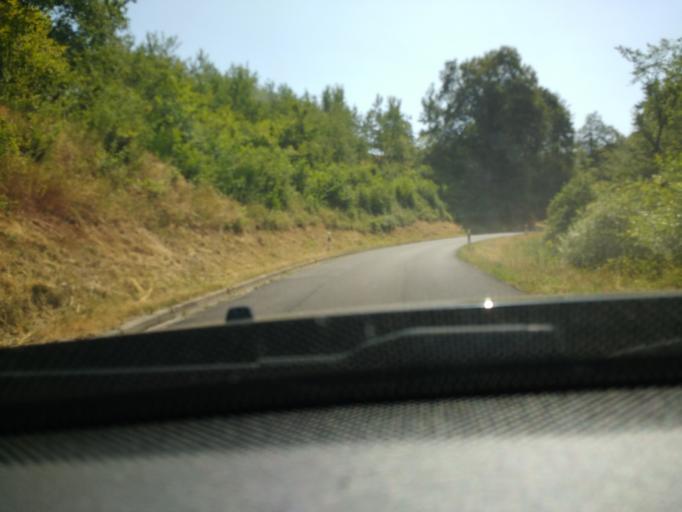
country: DE
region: Rheinland-Pfalz
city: Meerfeld
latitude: 50.0864
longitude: 6.7530
